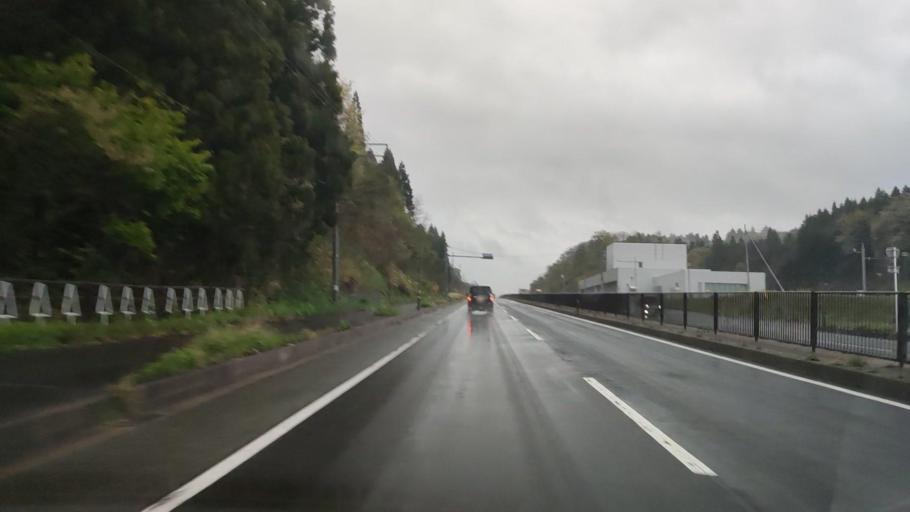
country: JP
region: Akita
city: Akita
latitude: 39.6605
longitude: 140.1932
